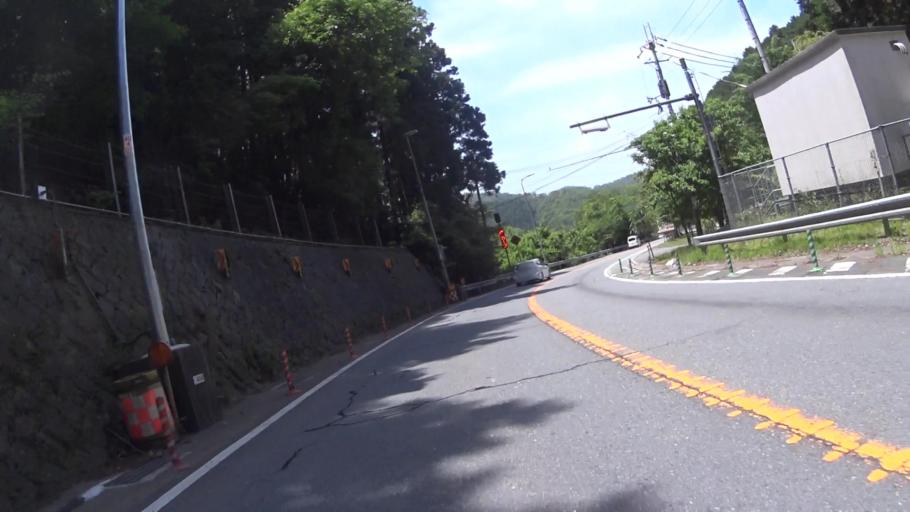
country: JP
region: Kyoto
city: Kameoka
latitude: 35.1225
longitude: 135.4394
